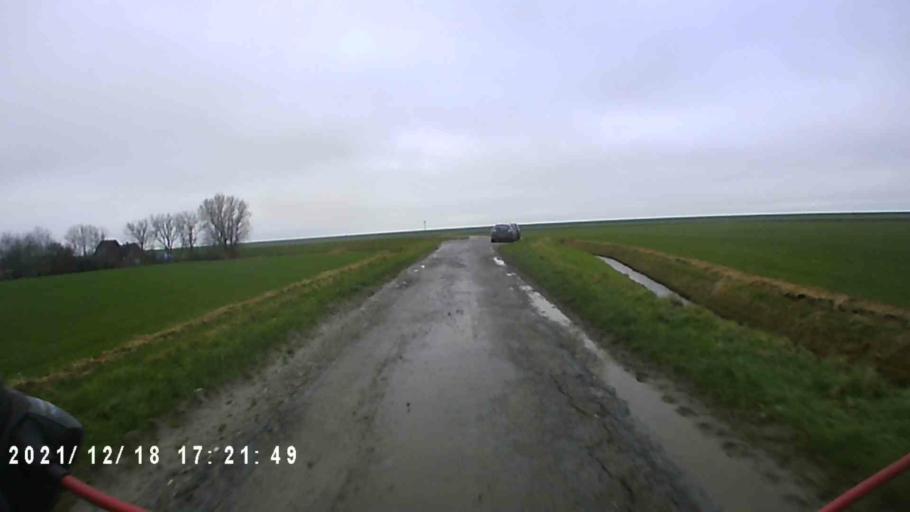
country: NL
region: Friesland
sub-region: Gemeente Dongeradeel
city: Holwerd
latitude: 53.3640
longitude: 5.8738
